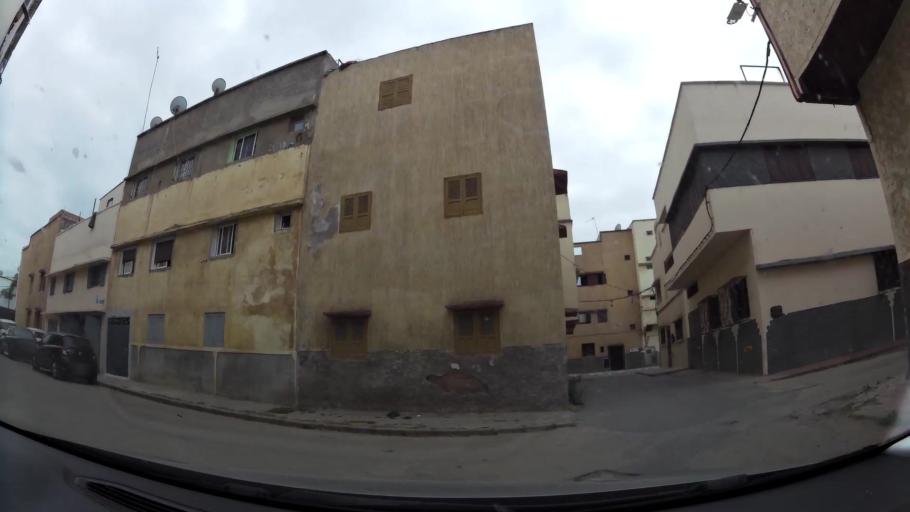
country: MA
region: Rabat-Sale-Zemmour-Zaer
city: Sale
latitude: 34.0317
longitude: -6.7978
